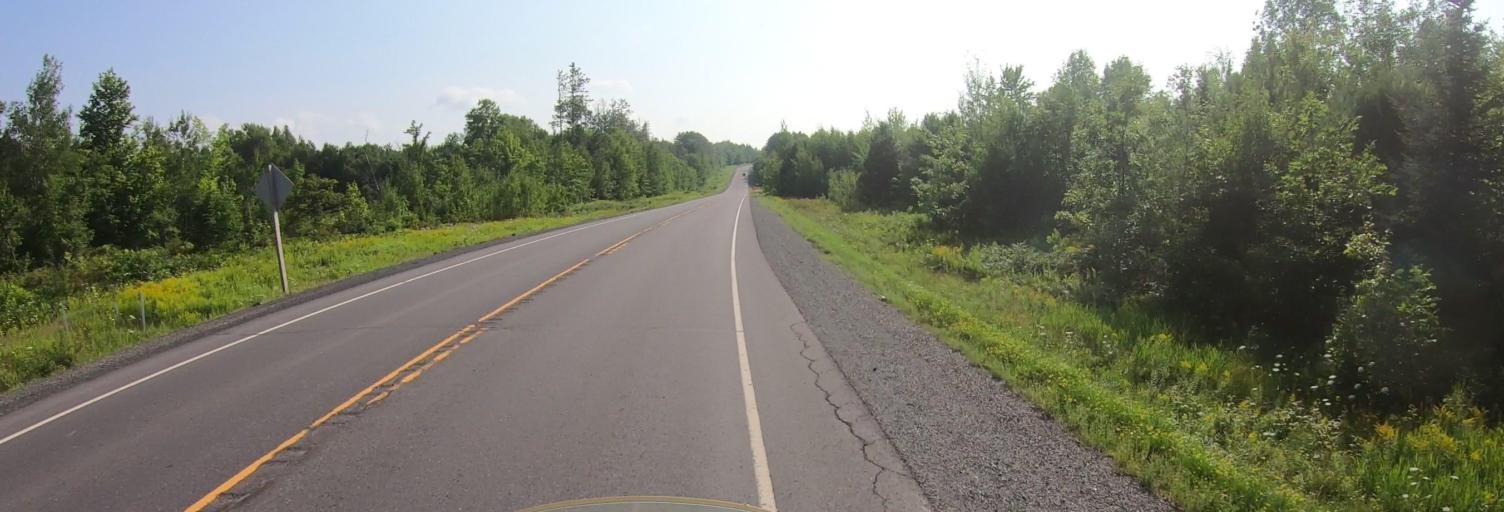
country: US
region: Wisconsin
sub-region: Iron County
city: Hurley
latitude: 46.4221
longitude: -90.2612
